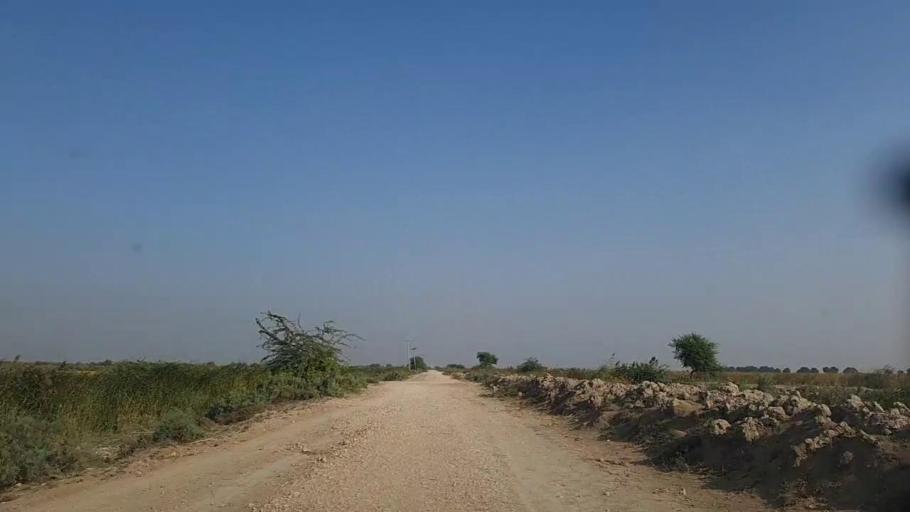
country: PK
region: Sindh
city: Jati
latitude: 24.4601
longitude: 68.2955
